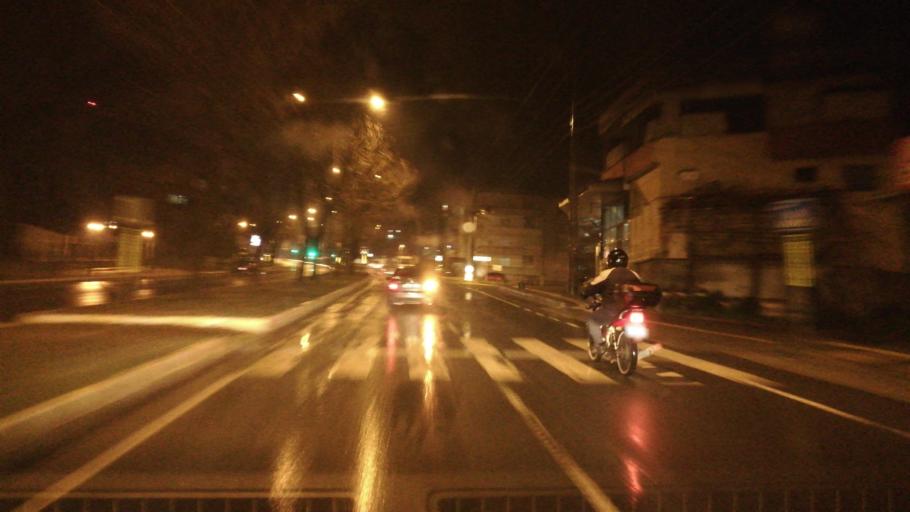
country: TR
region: Kahramanmaras
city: Kahramanmaras
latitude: 37.5846
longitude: 36.9459
